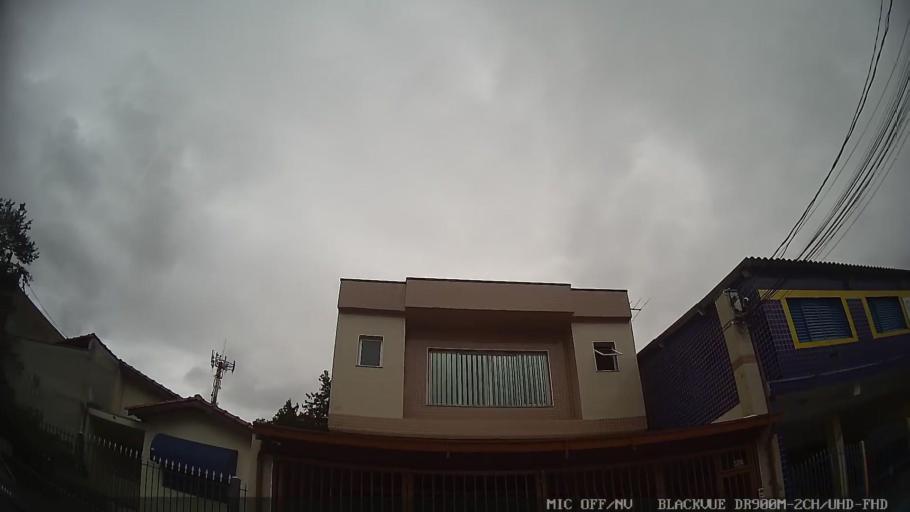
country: BR
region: Sao Paulo
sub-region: Osasco
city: Osasco
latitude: -23.5043
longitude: -46.7398
